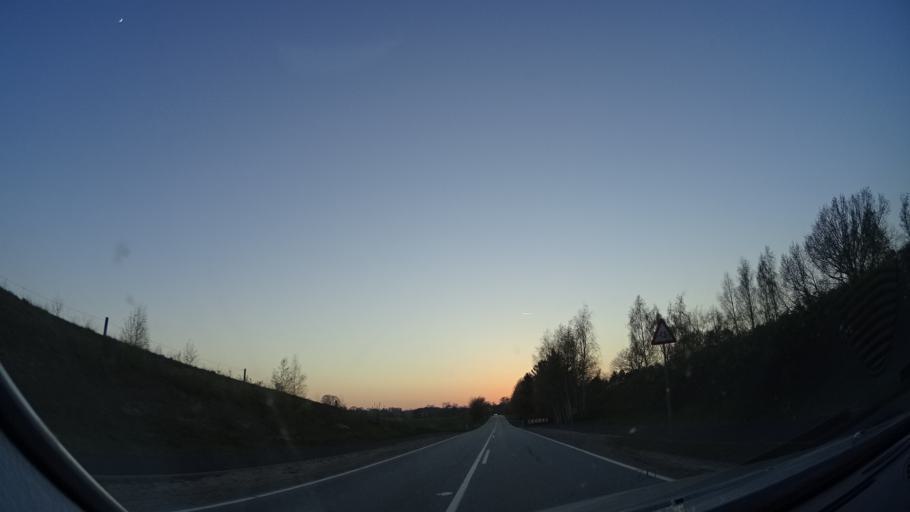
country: DK
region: Zealand
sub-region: Lejre Kommune
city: Ejby
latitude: 55.6710
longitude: 11.8753
